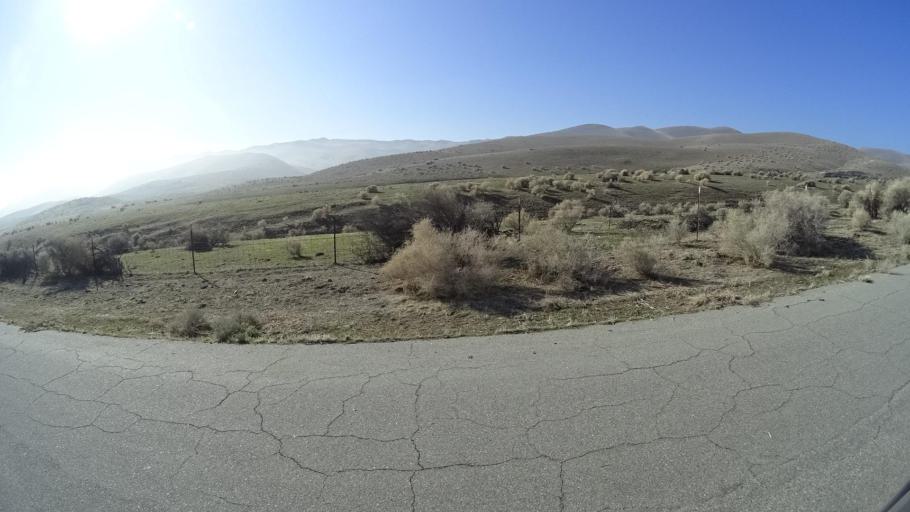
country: US
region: California
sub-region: Kern County
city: Taft Heights
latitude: 35.2288
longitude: -119.6422
